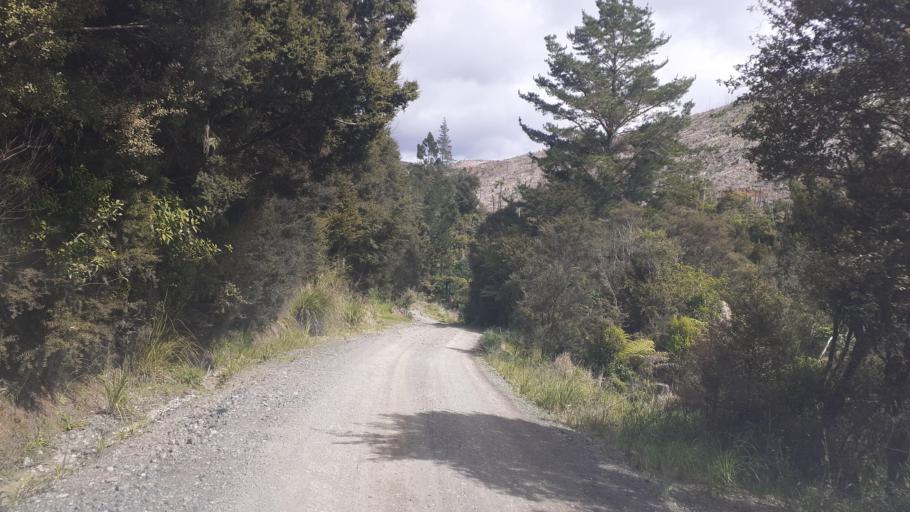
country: NZ
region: Northland
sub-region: Far North District
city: Moerewa
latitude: -35.5833
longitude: 173.9391
